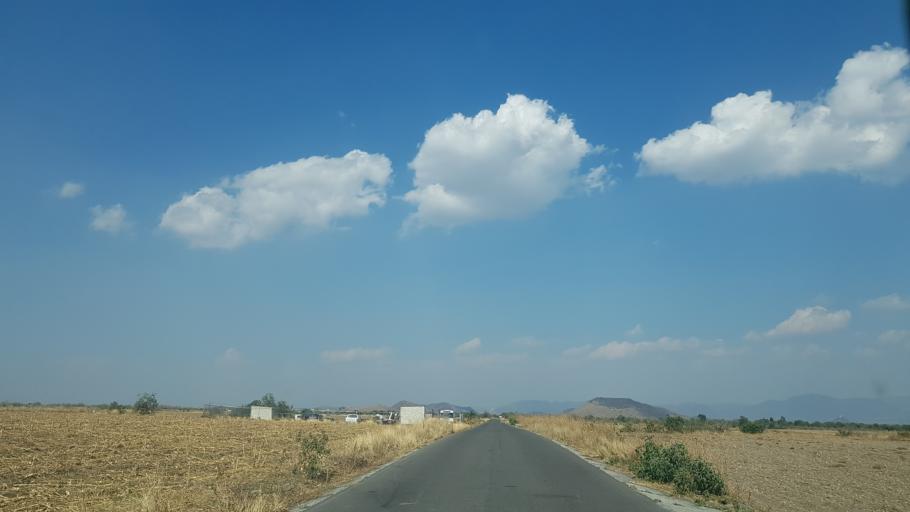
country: MX
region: Puebla
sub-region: Atlixco
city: Colonia Agricola de Ocotepec (Colonia San Jose)
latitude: 18.9209
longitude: -98.5153
